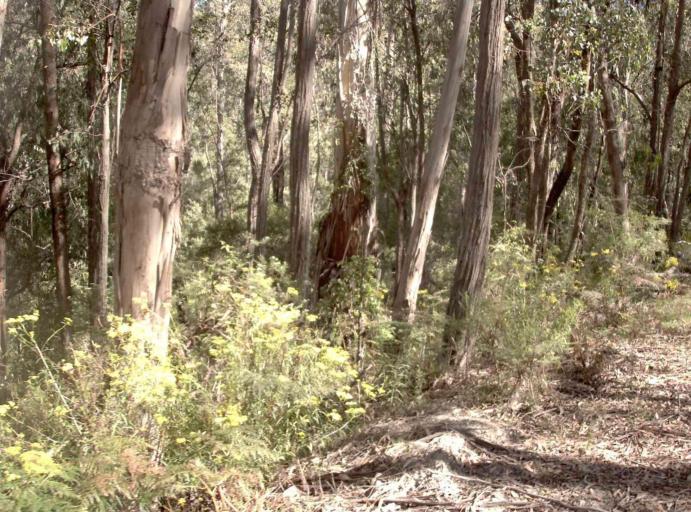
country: AU
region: New South Wales
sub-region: Bombala
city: Bombala
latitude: -37.2982
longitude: 148.7085
